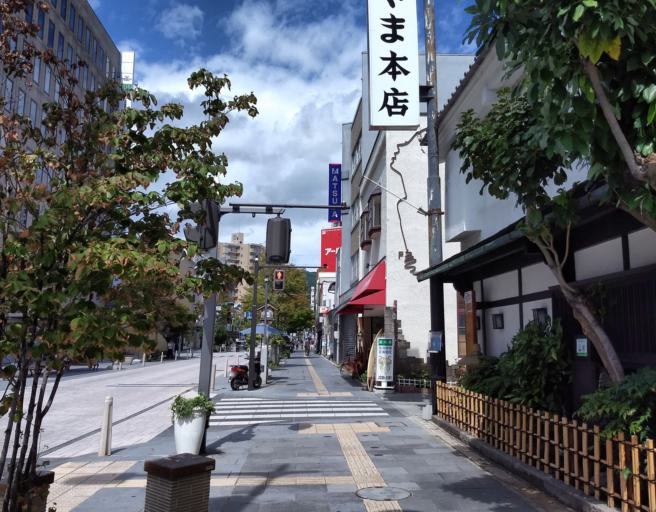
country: JP
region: Nagano
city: Nagano-shi
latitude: 36.6522
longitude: 138.1874
